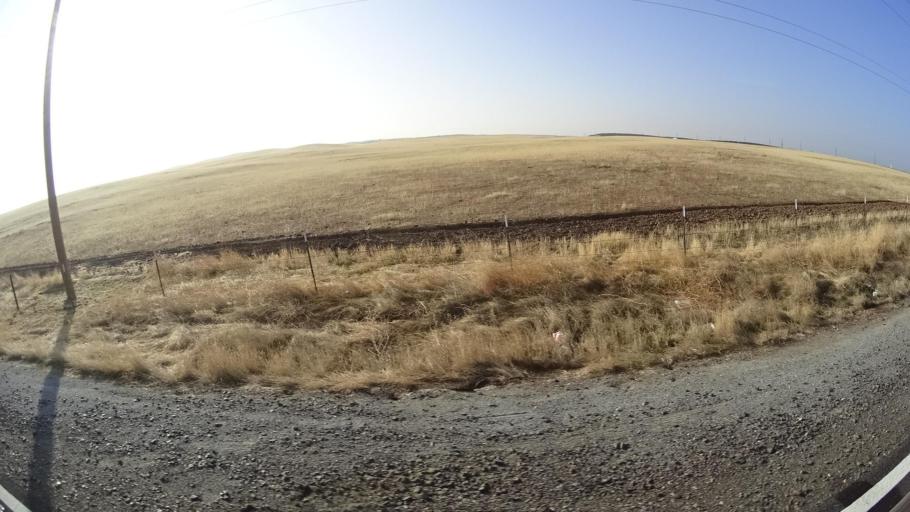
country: US
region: California
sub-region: Tulare County
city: Richgrove
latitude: 35.7620
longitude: -119.0483
